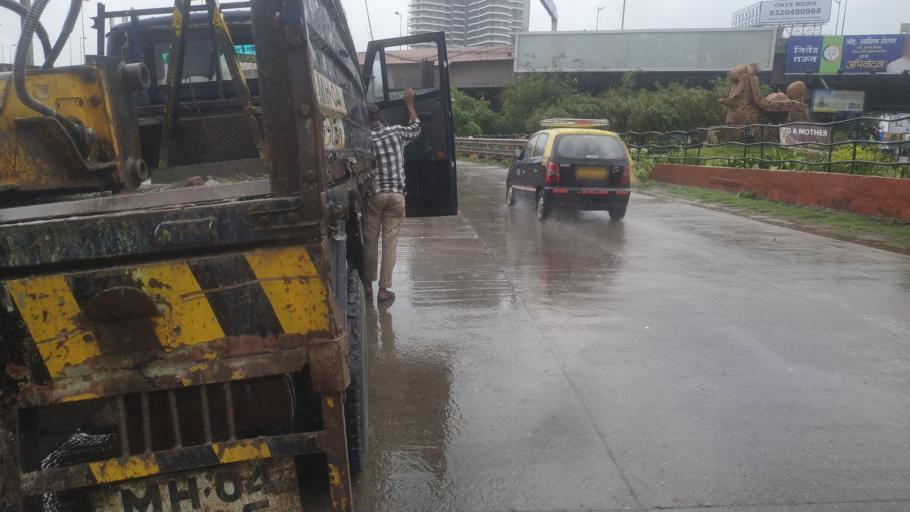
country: IN
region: Maharashtra
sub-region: Mumbai Suburban
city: Mumbai
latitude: 19.0491
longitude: 72.8381
